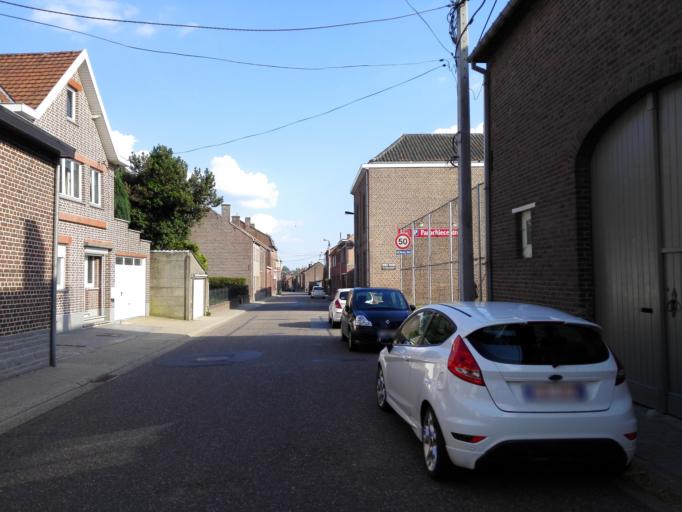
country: BE
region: Flanders
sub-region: Provincie Vlaams-Brabant
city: Tienen
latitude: 50.8283
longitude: 4.9917
